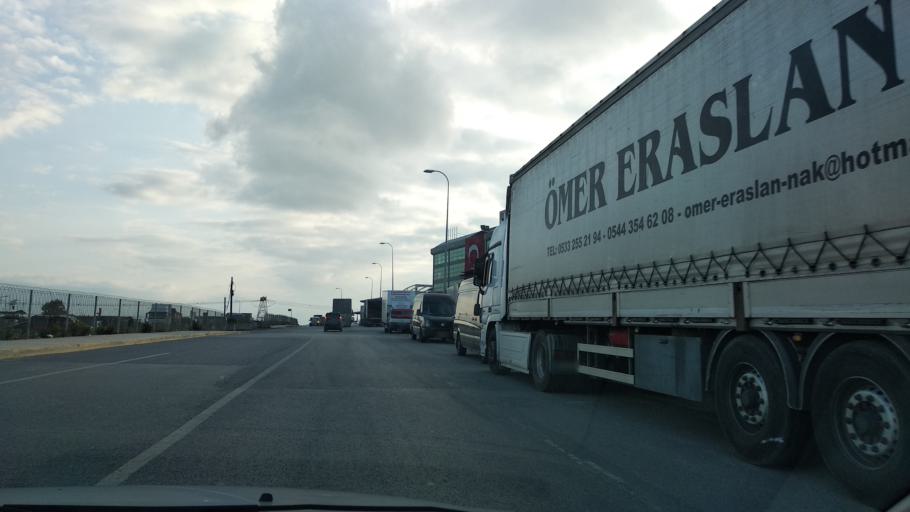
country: TR
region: Istanbul
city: Icmeler
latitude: 40.9206
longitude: 29.3489
